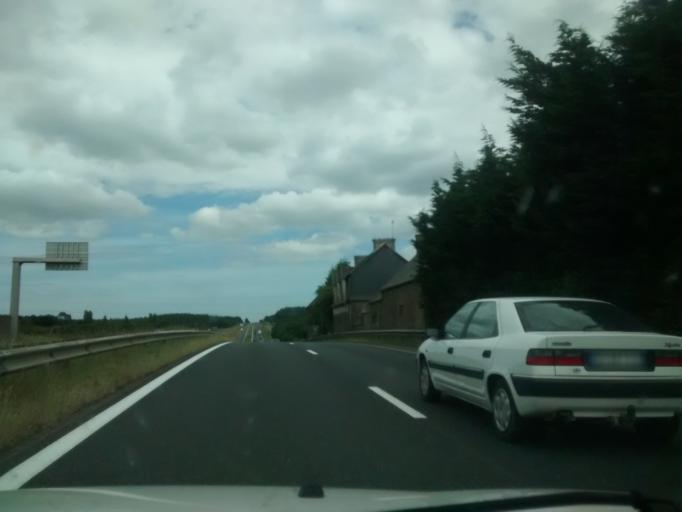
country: FR
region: Brittany
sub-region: Departement des Cotes-d'Armor
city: Saint-Agathon
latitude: 48.5433
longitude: -3.0826
